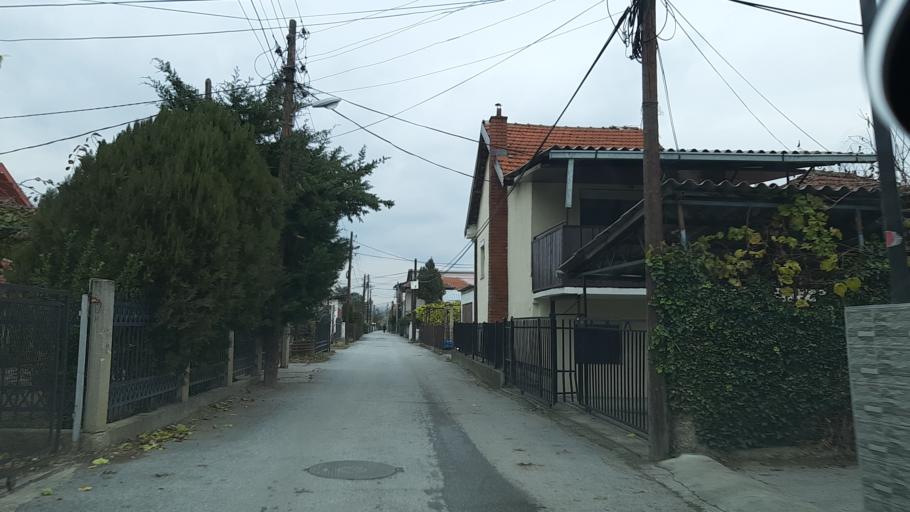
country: MK
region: Kisela Voda
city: Usje
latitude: 41.9775
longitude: 21.4775
